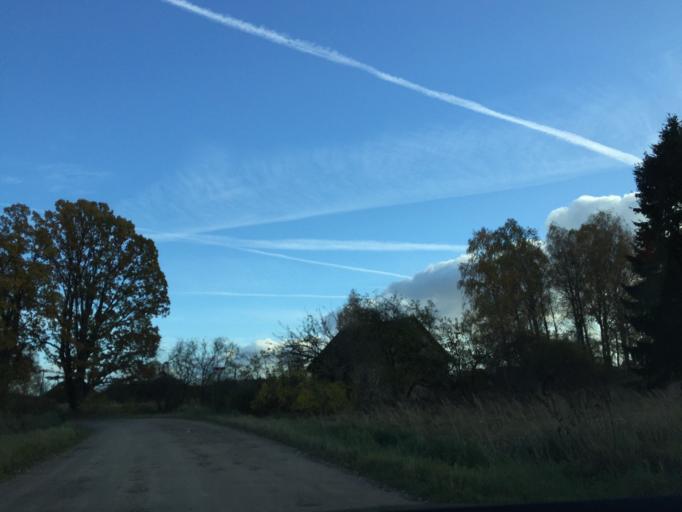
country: LV
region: Ogre
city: Jumprava
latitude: 56.7640
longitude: 24.9789
